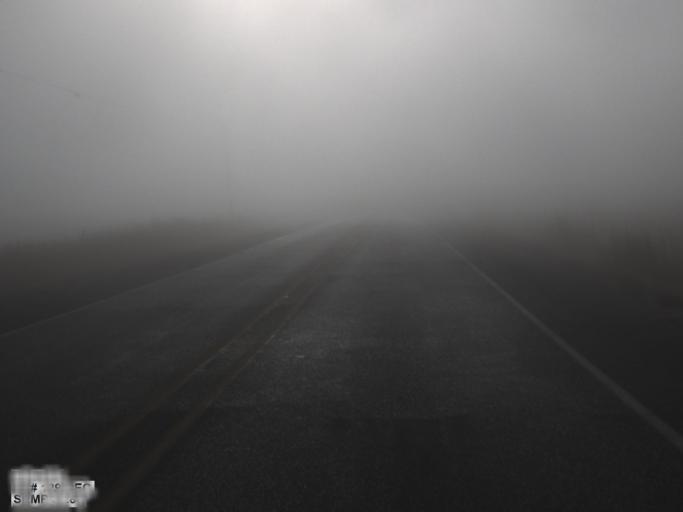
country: US
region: Washington
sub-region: Asotin County
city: Asotin
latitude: 46.3189
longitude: -117.0402
